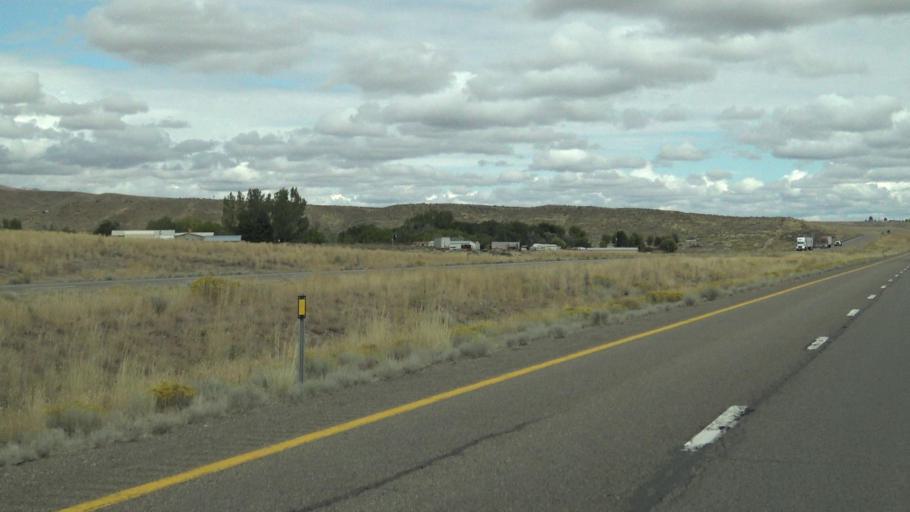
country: US
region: Nevada
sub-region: Elko County
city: Elko
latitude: 40.9022
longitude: -115.7033
